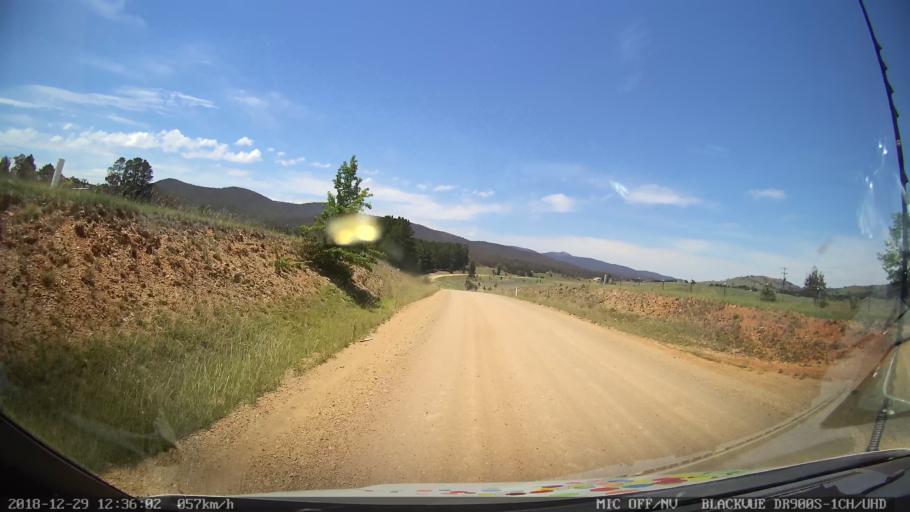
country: AU
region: Australian Capital Territory
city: Macarthur
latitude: -35.5671
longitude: 149.2245
